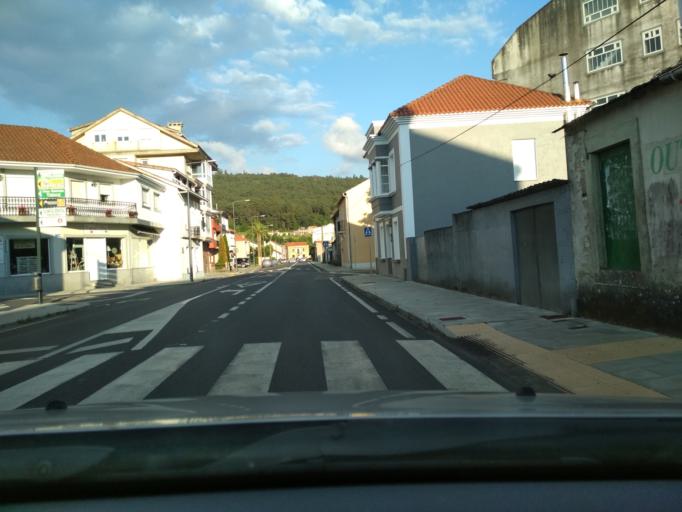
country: ES
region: Galicia
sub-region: Provincia da Coruna
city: Outes
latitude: 42.8420
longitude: -8.9054
